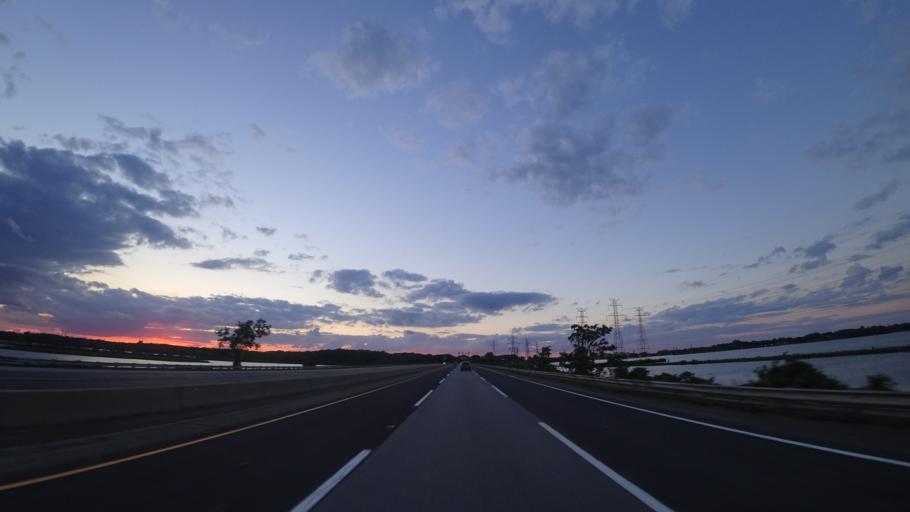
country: US
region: Indiana
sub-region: Lake County
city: Whiting
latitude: 41.6690
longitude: -87.5202
